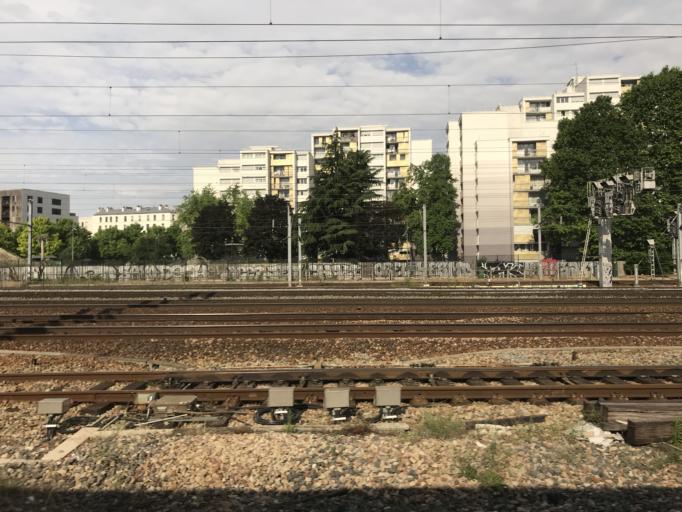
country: FR
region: Ile-de-France
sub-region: Paris
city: Saint-Ouen
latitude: 48.8957
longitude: 2.3549
